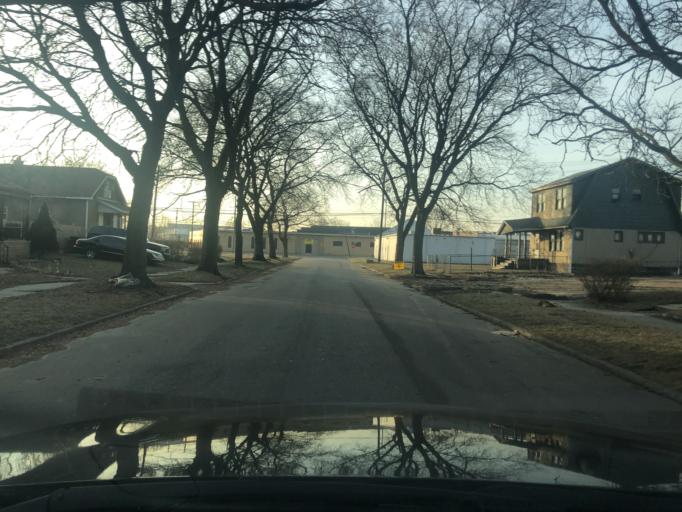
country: US
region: Michigan
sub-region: Wayne County
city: Highland Park
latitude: 42.4040
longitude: -83.1249
